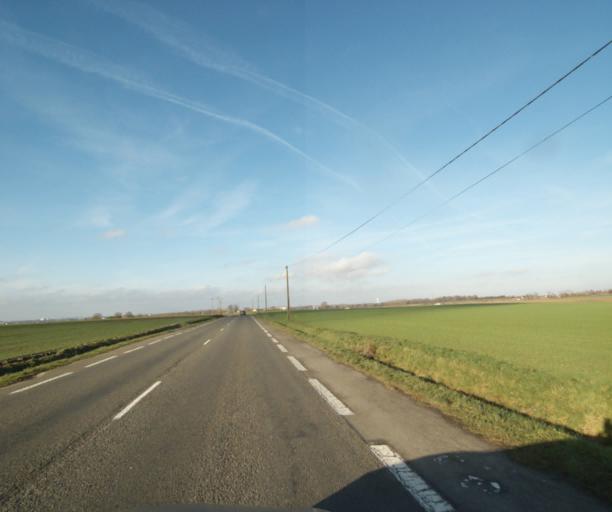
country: FR
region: Nord-Pas-de-Calais
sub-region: Departement du Nord
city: Preseau
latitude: 50.3236
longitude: 3.5635
